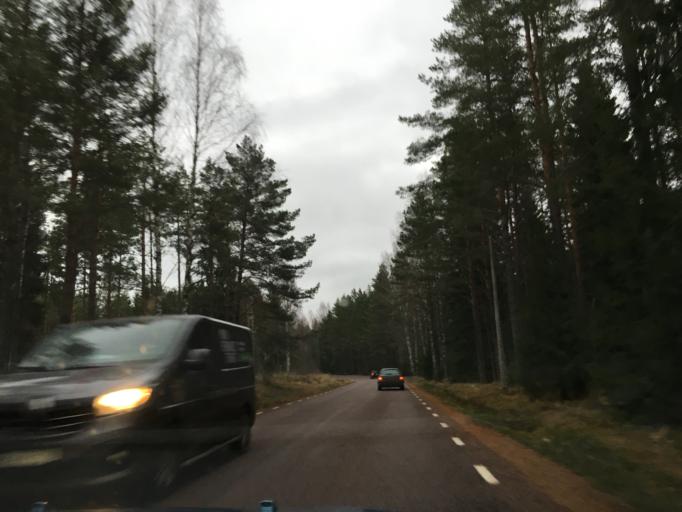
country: SE
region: Uppsala
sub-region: Alvkarleby Kommun
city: AElvkarleby
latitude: 60.6224
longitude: 17.4657
